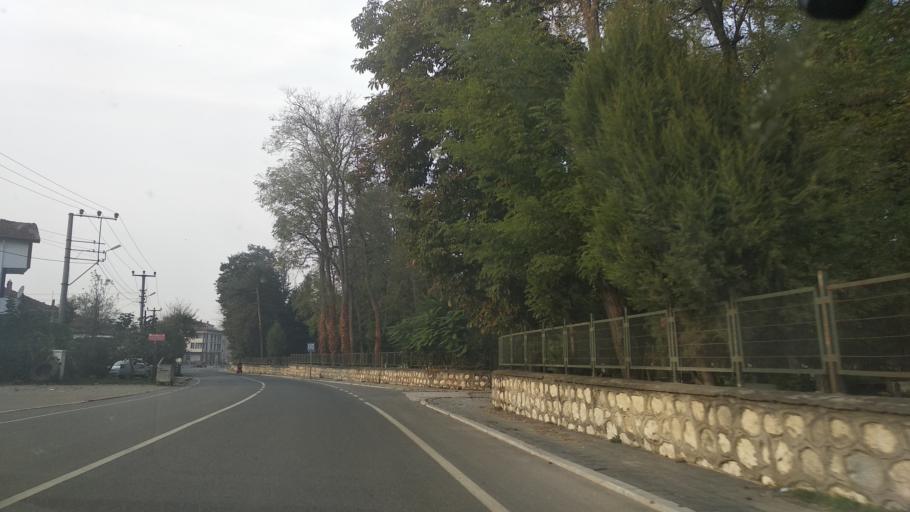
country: TR
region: Duzce
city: Duzce
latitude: 40.8279
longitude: 31.1731
